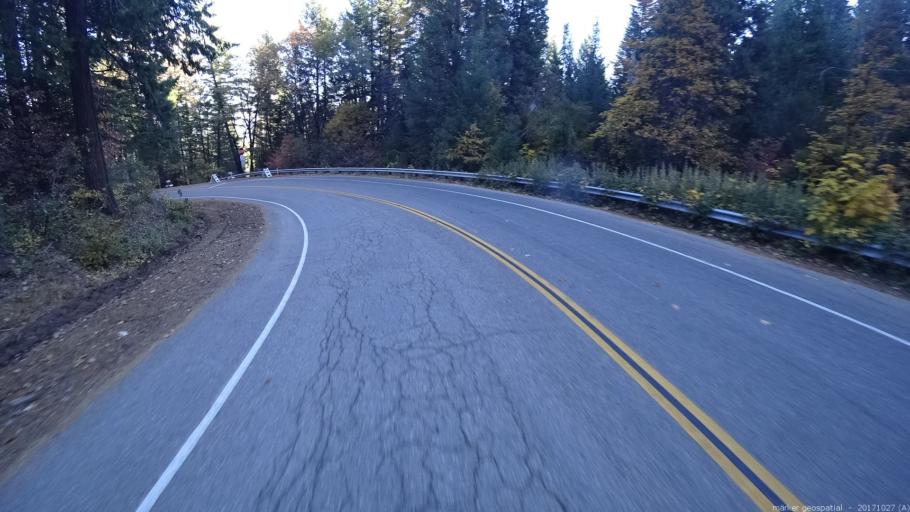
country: US
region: California
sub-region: Shasta County
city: Burney
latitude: 40.9878
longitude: -121.9227
